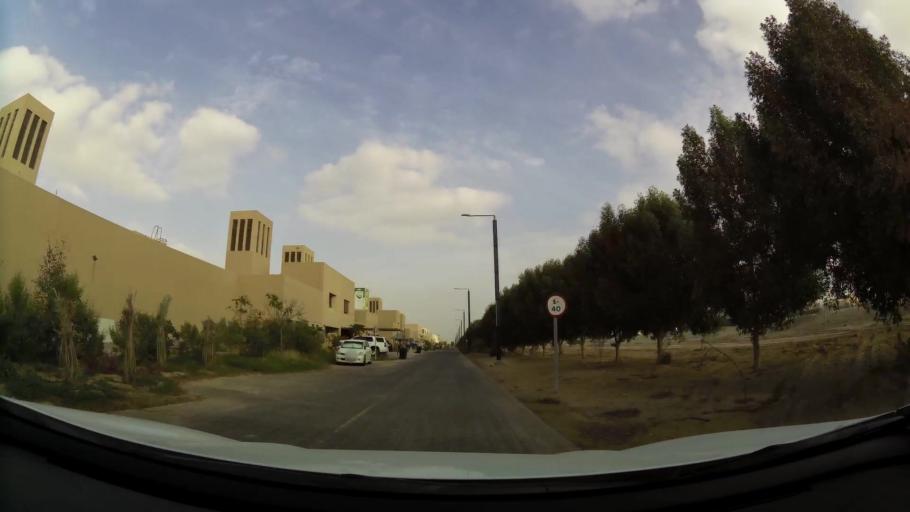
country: AE
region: Abu Dhabi
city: Abu Dhabi
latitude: 24.5001
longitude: 54.5966
